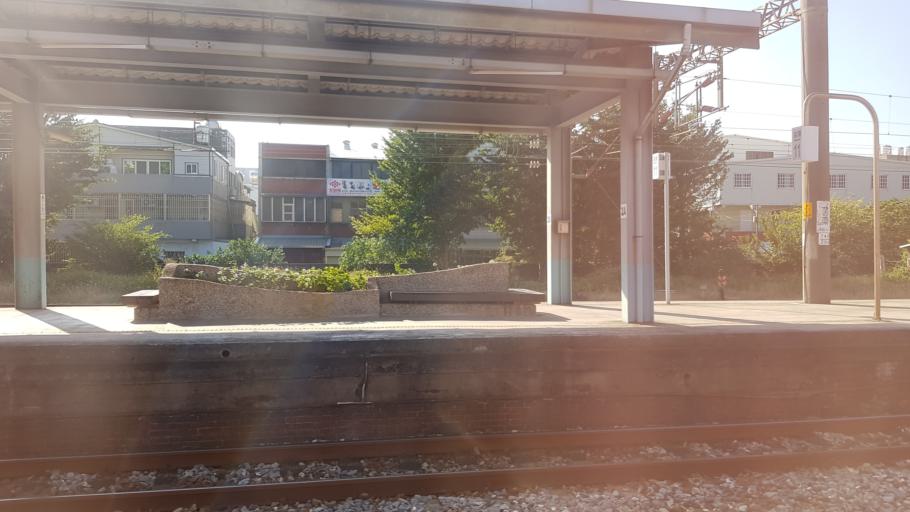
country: TW
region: Taiwan
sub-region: Miaoli
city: Miaoli
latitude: 24.5708
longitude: 120.8219
